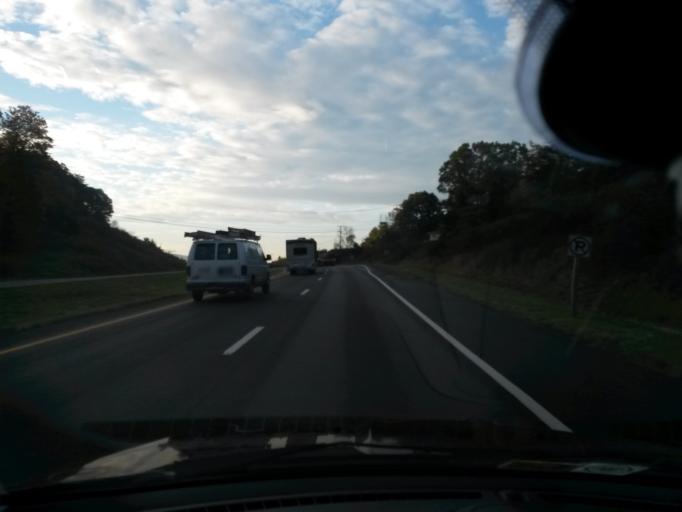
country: US
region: Virginia
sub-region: Botetourt County
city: Cloverdale
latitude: 37.3639
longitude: -79.8867
